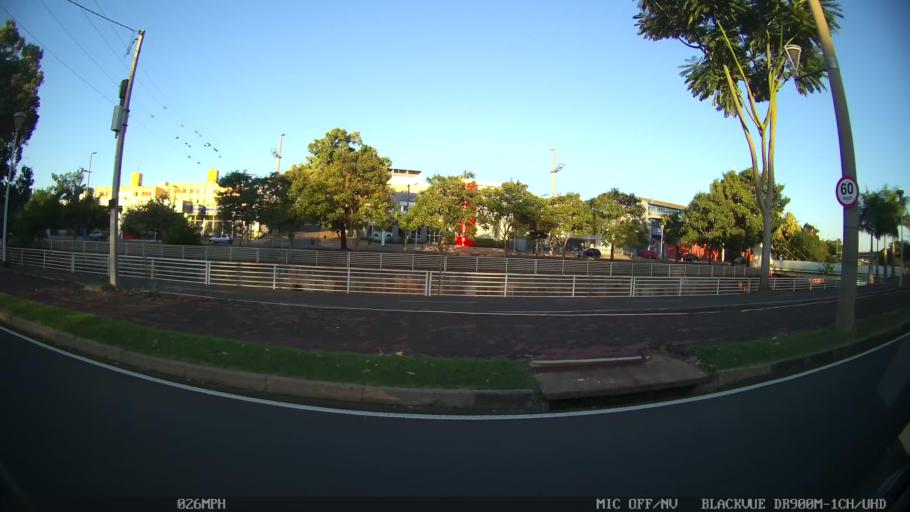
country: BR
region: Sao Paulo
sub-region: Sao Jose Do Rio Preto
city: Sao Jose do Rio Preto
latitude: -20.8018
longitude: -49.3782
